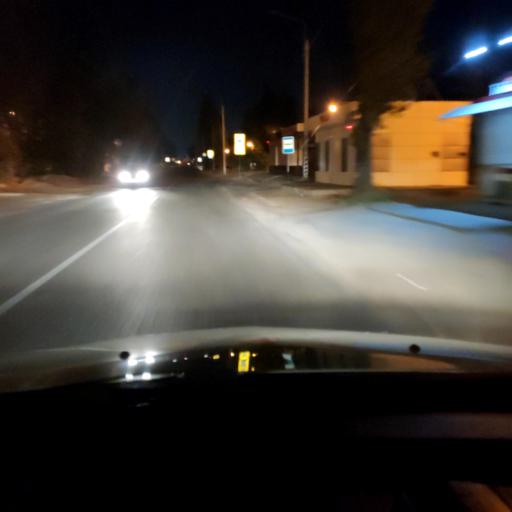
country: RU
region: Voronezj
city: Maslovka
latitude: 51.5502
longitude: 39.2348
